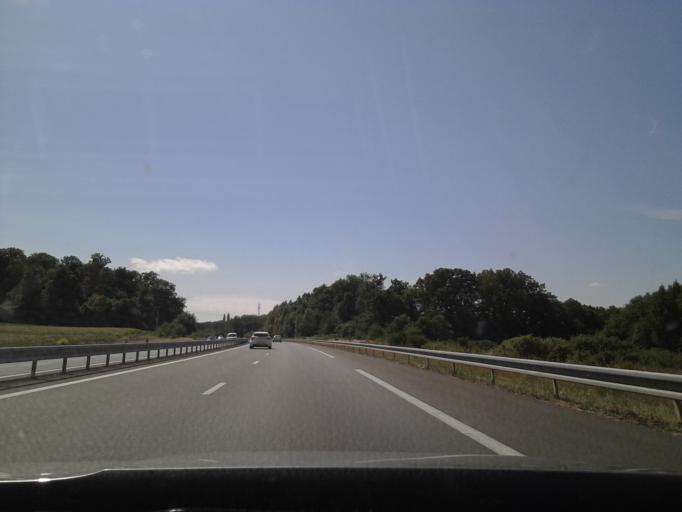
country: FR
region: Pays de la Loire
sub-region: Departement de la Sarthe
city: Ecommoy
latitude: 47.8555
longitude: 0.2974
